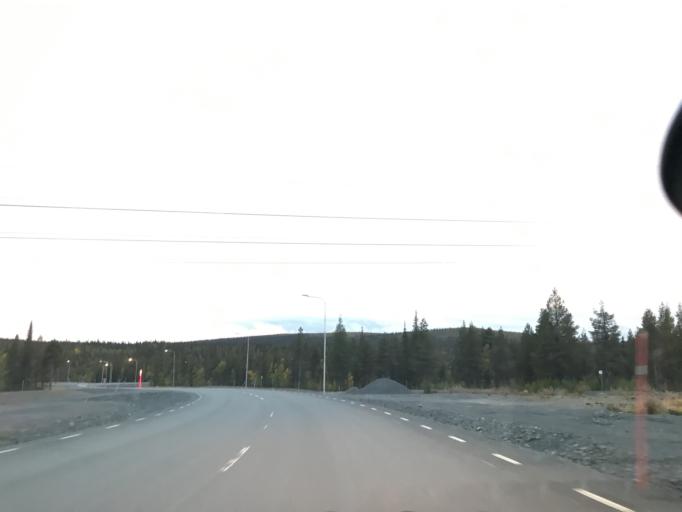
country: SE
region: Norrbotten
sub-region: Gallivare Kommun
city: Malmberget
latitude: 67.6970
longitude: 20.8119
